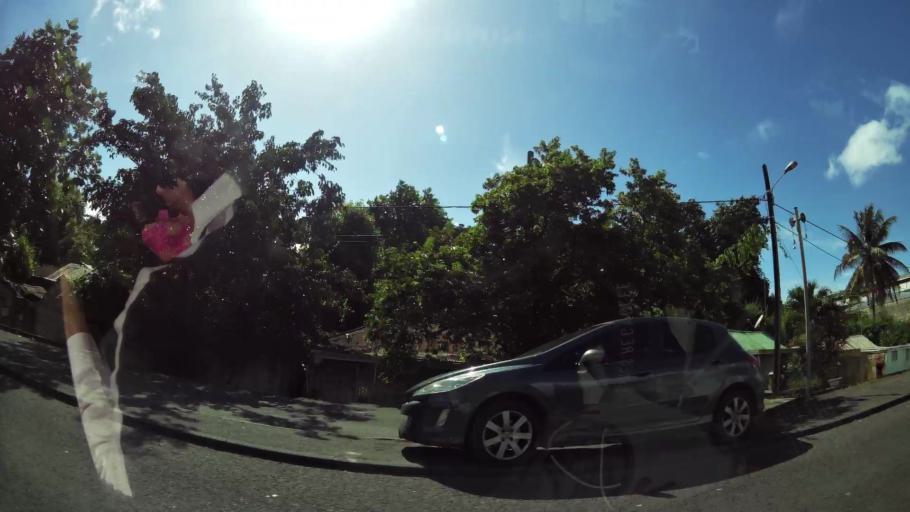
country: GP
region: Guadeloupe
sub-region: Guadeloupe
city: Pointe-a-Pitre
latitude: 16.2385
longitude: -61.5289
